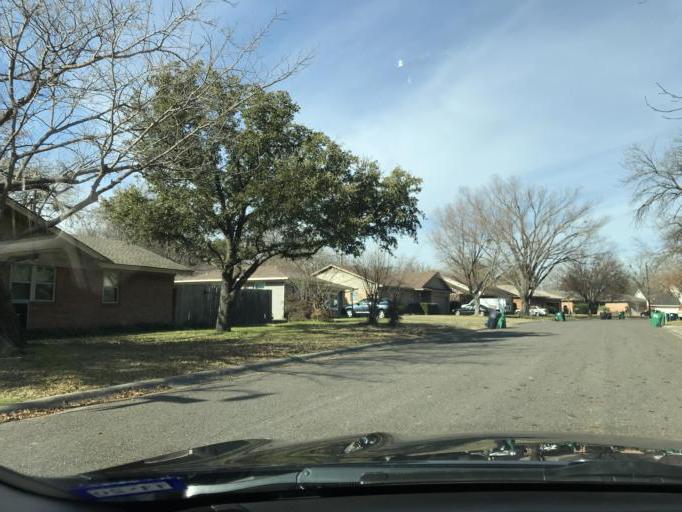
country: US
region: Texas
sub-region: Denton County
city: Denton
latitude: 33.2314
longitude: -97.1464
